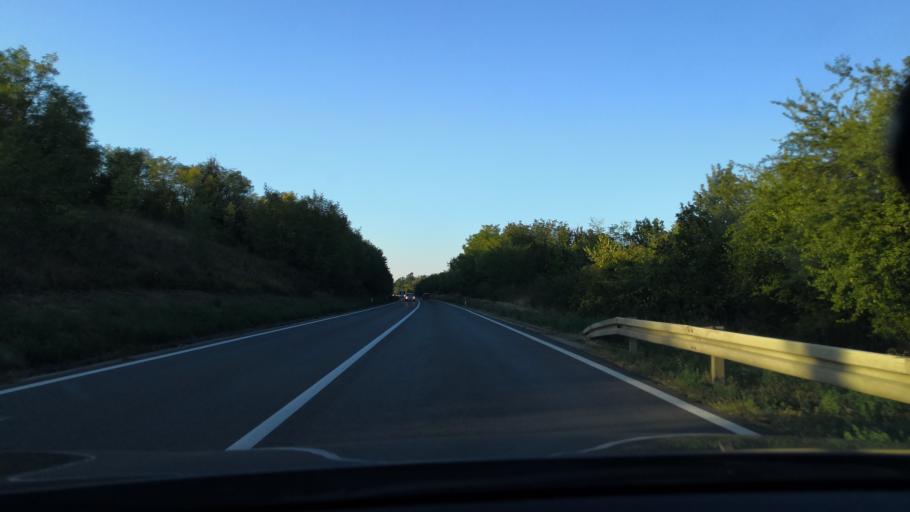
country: RS
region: Central Serbia
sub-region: Belgrade
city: Sopot
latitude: 44.5242
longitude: 20.6549
